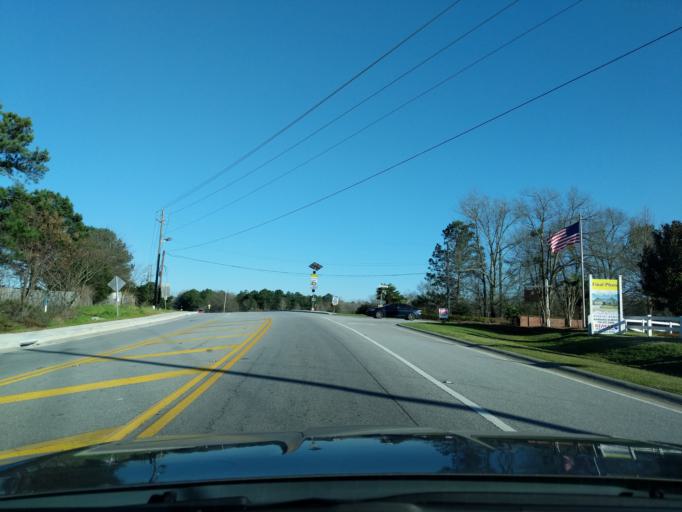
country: US
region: Georgia
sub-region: Columbia County
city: Grovetown
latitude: 33.4523
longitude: -82.2233
